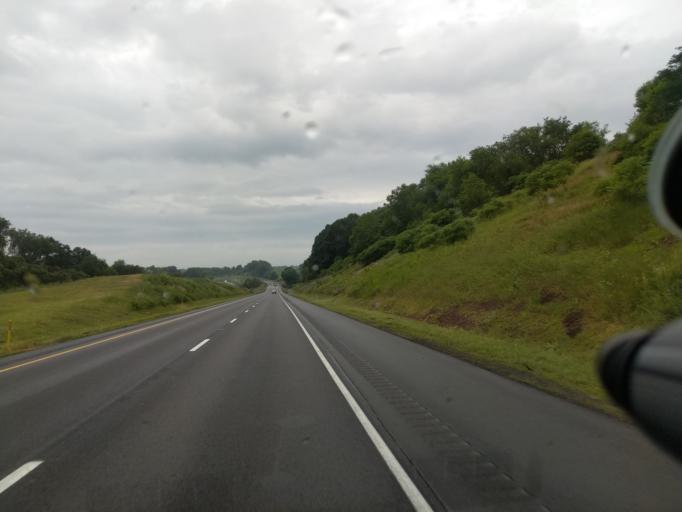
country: US
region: Pennsylvania
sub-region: Northumberland County
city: Milton
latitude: 41.0357
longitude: -76.8082
